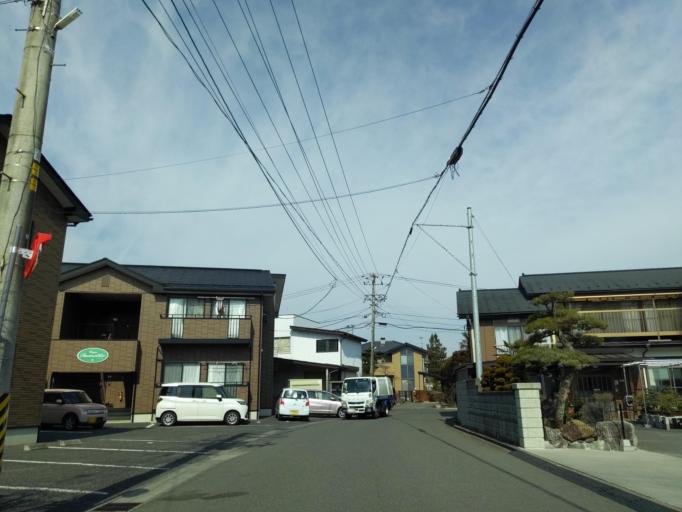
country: JP
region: Fukushima
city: Koriyama
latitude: 37.4254
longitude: 140.3554
